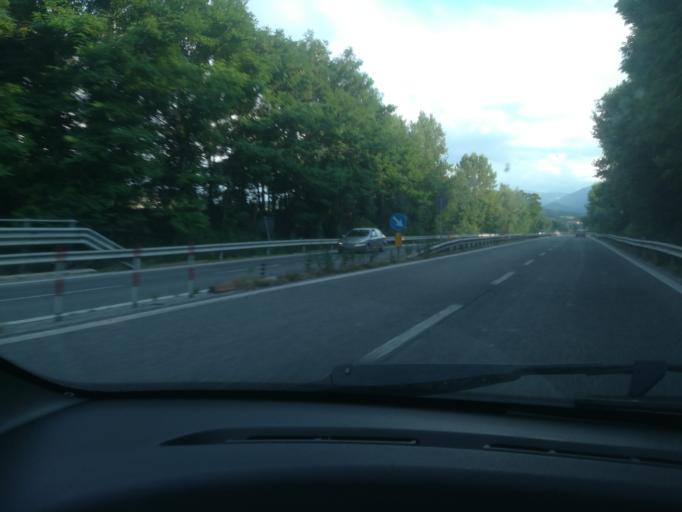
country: IT
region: The Marches
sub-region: Provincia di Macerata
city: Belforte del Chienti
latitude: 43.1767
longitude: 13.2494
